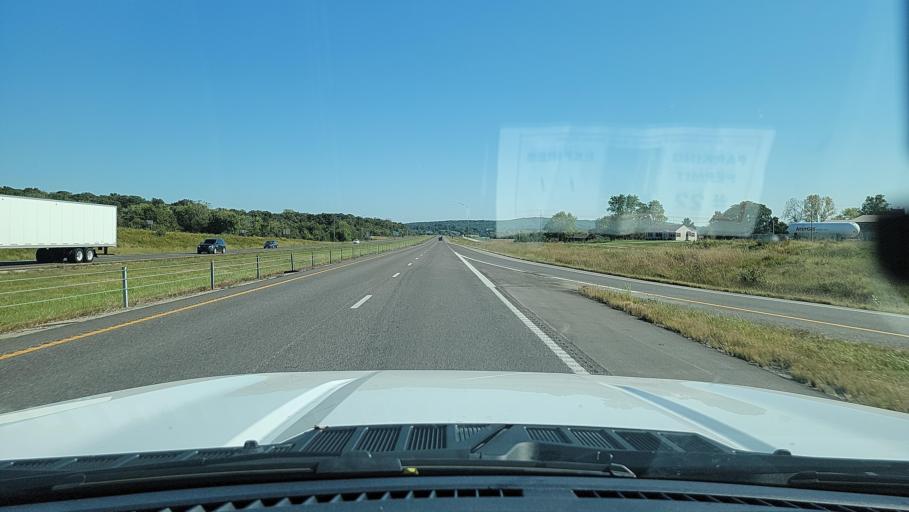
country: US
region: Missouri
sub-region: Sainte Genevieve County
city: Sainte Genevieve
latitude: 37.9355
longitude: -90.1214
